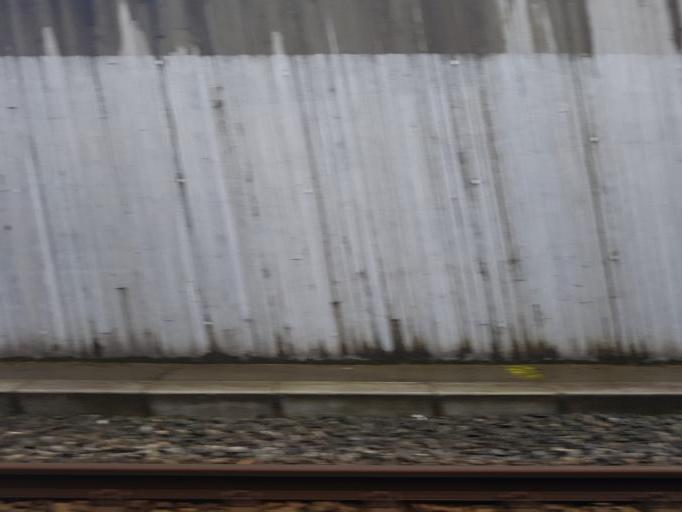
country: NO
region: Hordaland
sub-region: Bergen
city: Ytrebygda
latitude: 60.2925
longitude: 5.2390
